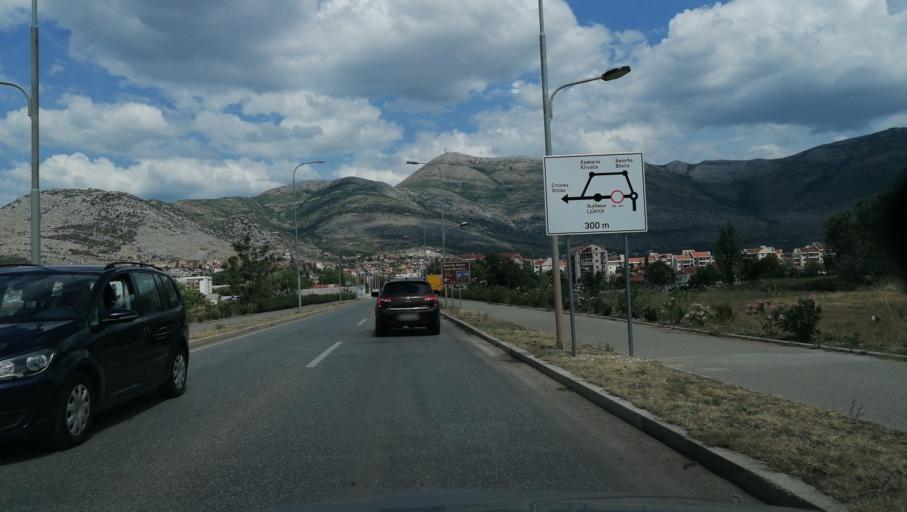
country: BA
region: Republika Srpska
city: Trebinje
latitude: 42.7026
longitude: 18.3433
